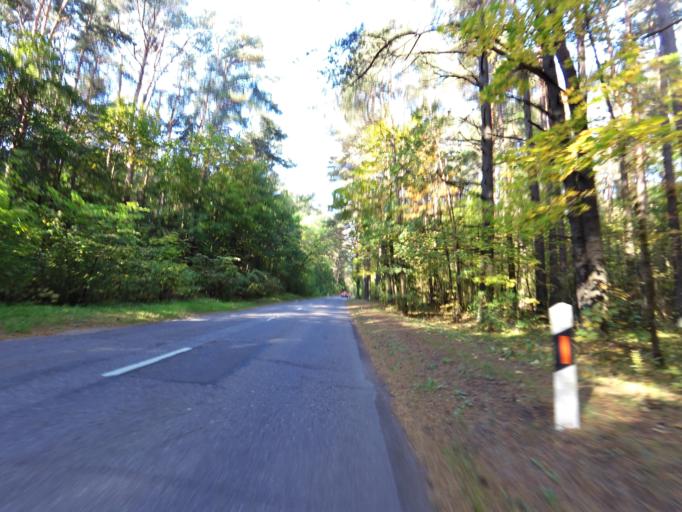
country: LT
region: Vilnius County
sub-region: Vilnius
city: Vilnius
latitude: 54.7318
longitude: 25.3052
